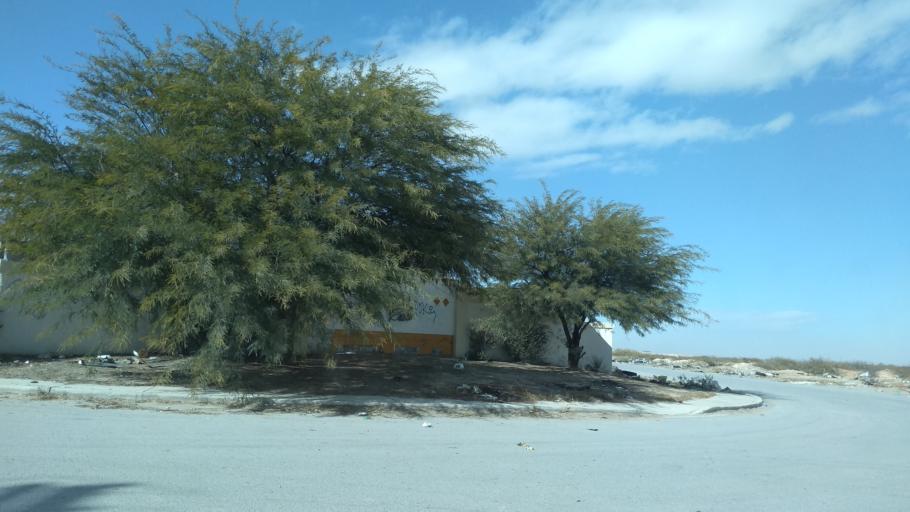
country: US
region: Texas
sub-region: El Paso County
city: San Elizario
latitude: 31.5762
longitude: -106.3273
